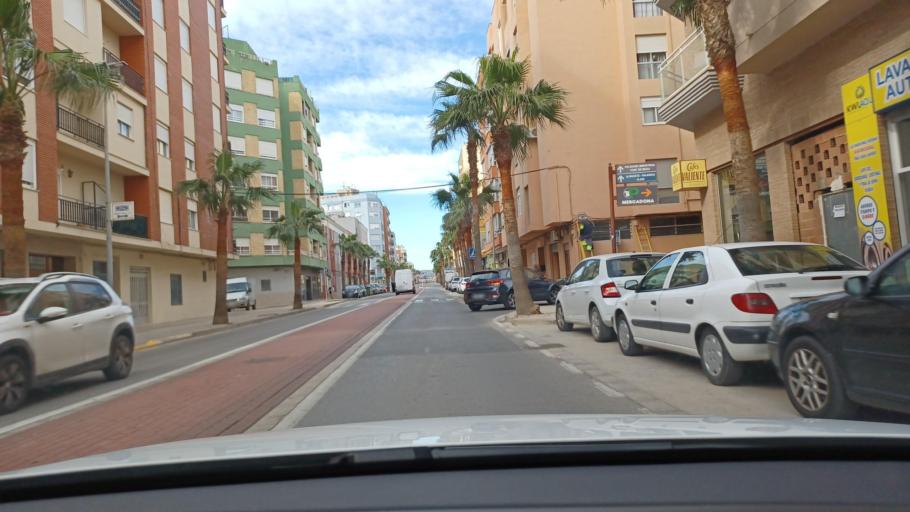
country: ES
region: Valencia
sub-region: Provincia de Valencia
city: Benifaio
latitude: 39.2885
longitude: -0.4228
